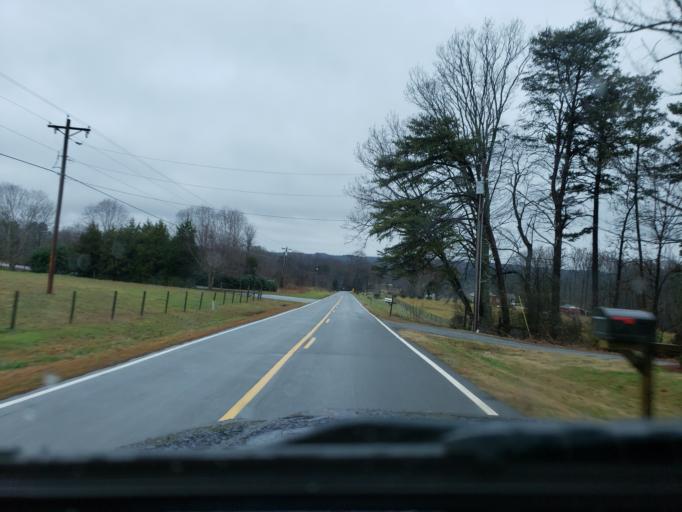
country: US
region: North Carolina
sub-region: Cleveland County
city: White Plains
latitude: 35.1764
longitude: -81.3646
